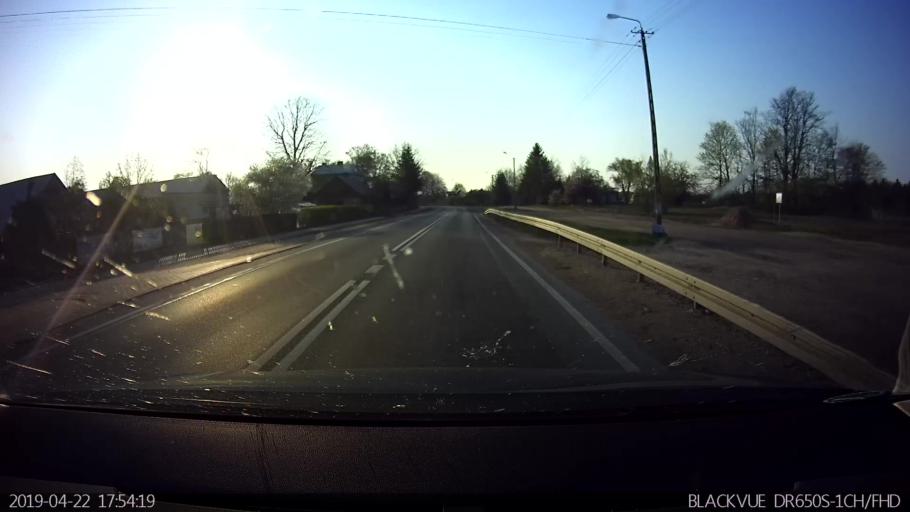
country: PL
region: Masovian Voivodeship
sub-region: Powiat wegrowski
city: Liw
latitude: 52.4566
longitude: 21.9415
